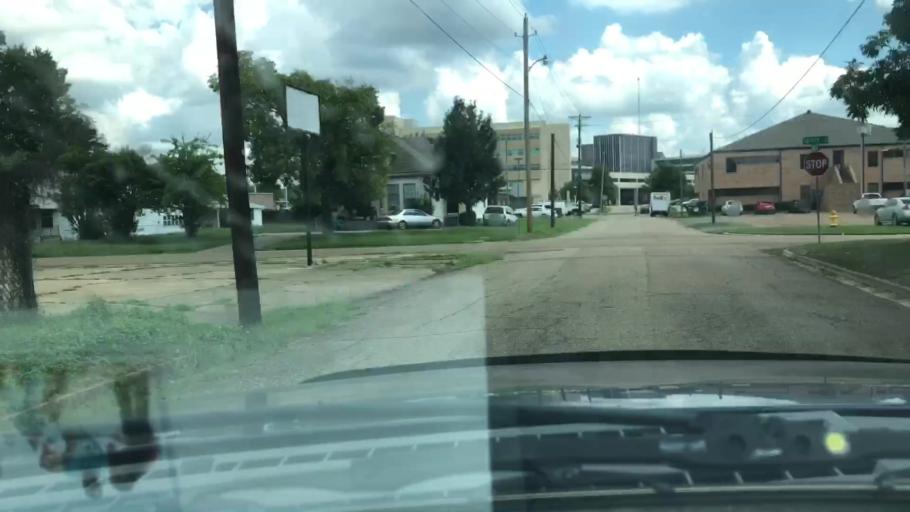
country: US
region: Texas
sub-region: Bowie County
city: Texarkana
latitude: 33.4273
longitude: -94.0512
